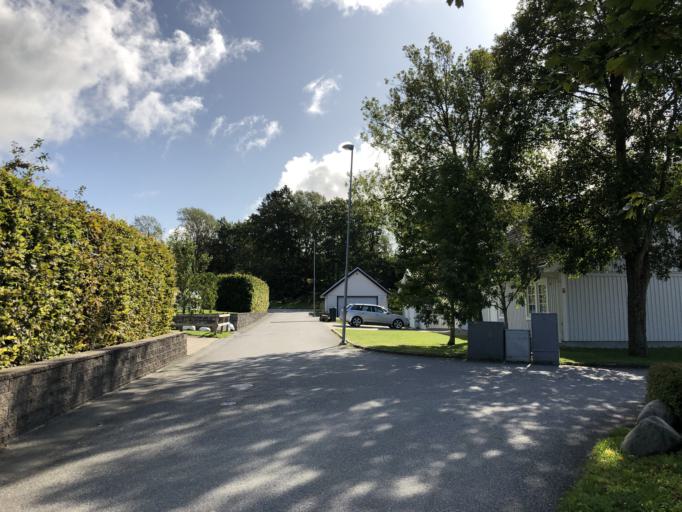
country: SE
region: Vaestra Goetaland
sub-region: Goteborg
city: Torslanda
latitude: 57.7433
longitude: 11.8274
